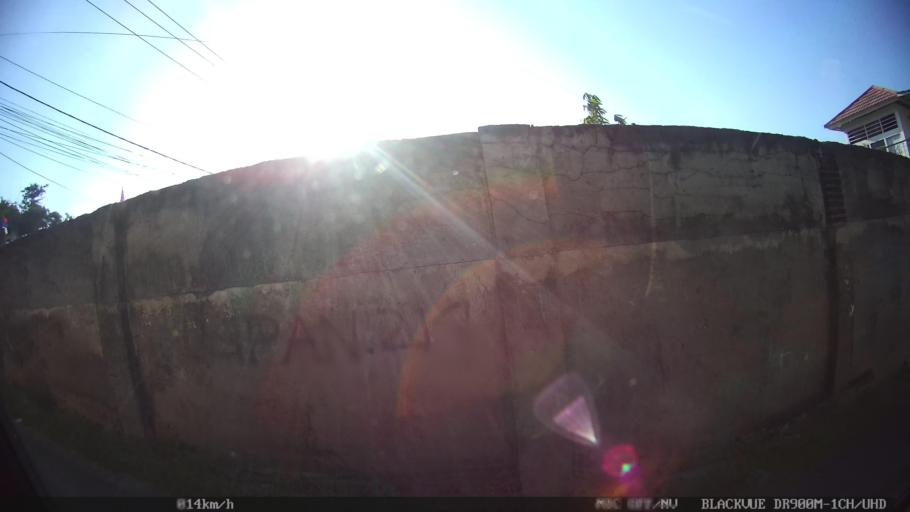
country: ID
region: Lampung
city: Kedaton
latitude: -5.3923
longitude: 105.2254
